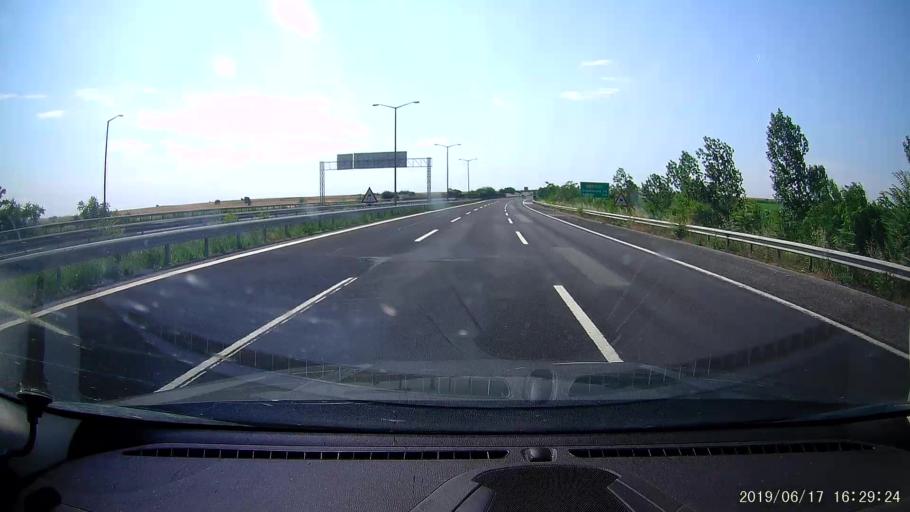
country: TR
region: Tekirdag
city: Beyazkoy
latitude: 41.3333
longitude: 27.6824
